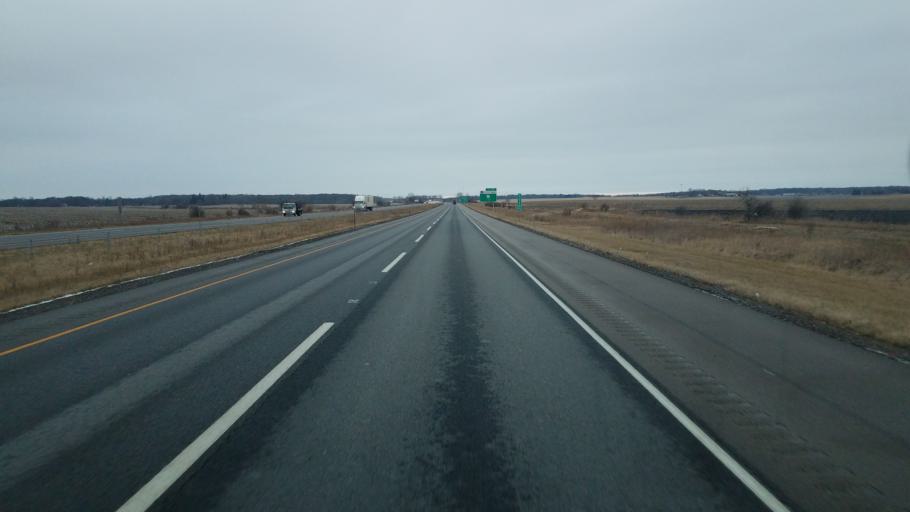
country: US
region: Illinois
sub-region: Kane County
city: Sugar Grove
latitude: 41.8087
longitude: -88.4412
